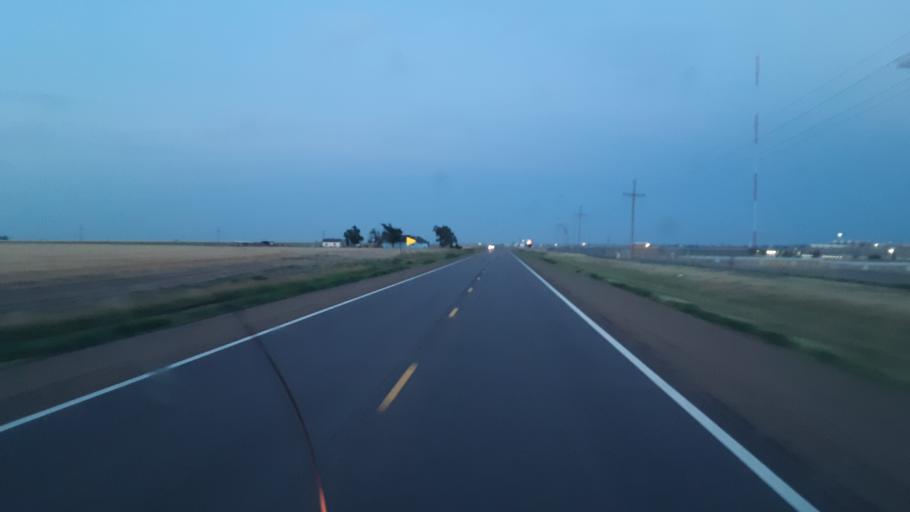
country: US
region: Kansas
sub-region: Finney County
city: Holcomb
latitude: 38.0034
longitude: -101.0350
